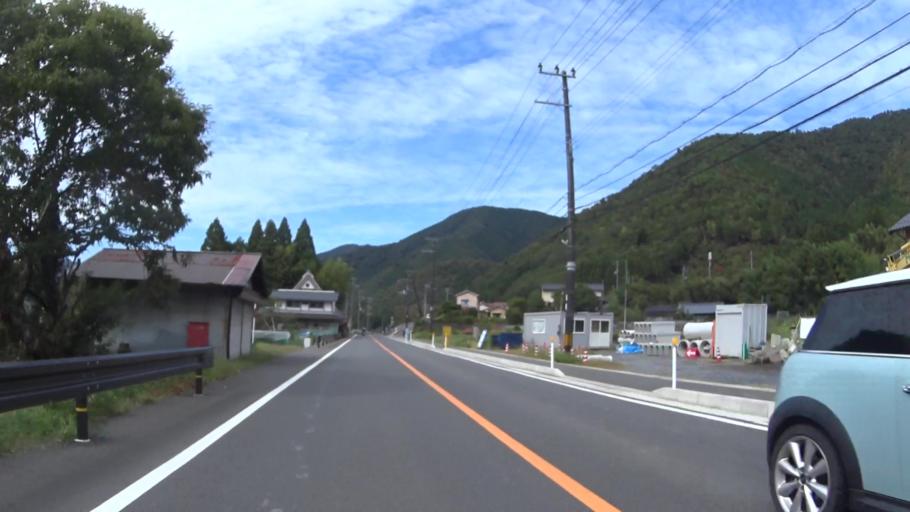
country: JP
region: Kyoto
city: Maizuru
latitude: 35.2755
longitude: 135.5449
